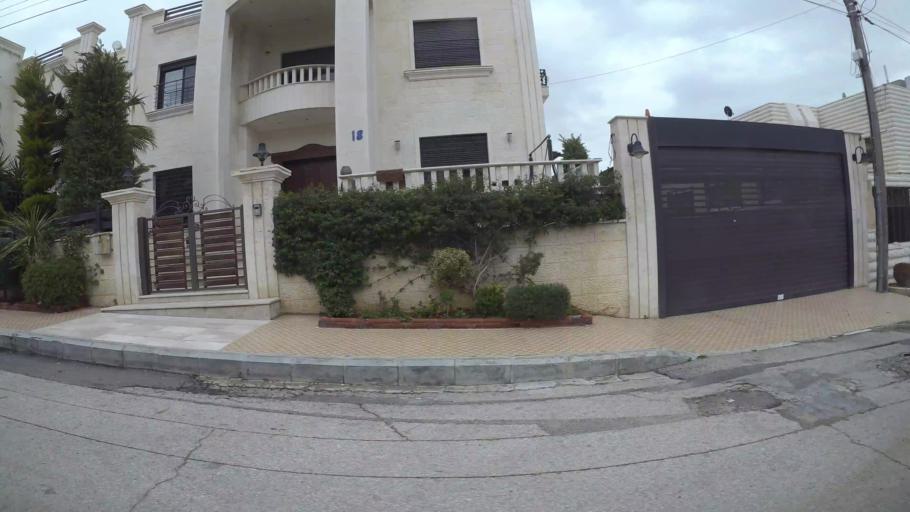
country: JO
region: Amman
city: Wadi as Sir
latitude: 31.9872
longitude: 35.8348
